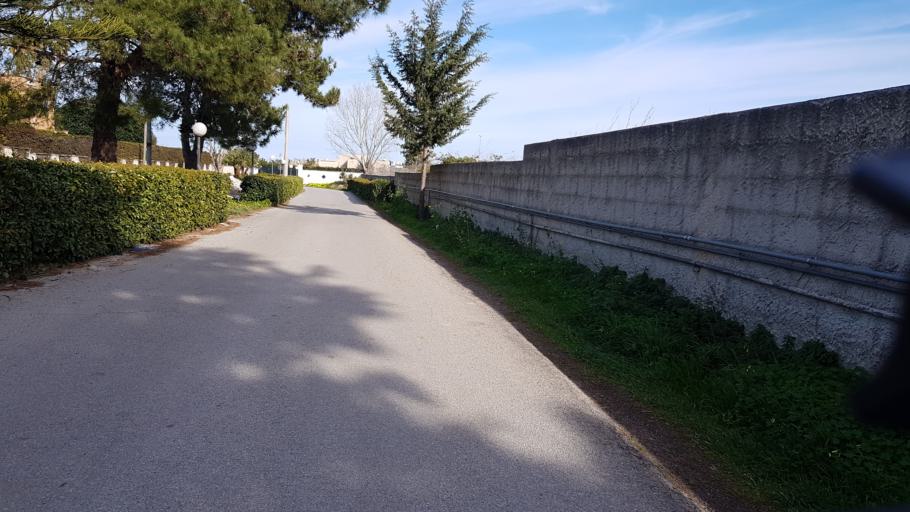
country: IT
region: Apulia
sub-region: Provincia di Brindisi
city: Brindisi
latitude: 40.6484
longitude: 17.9314
